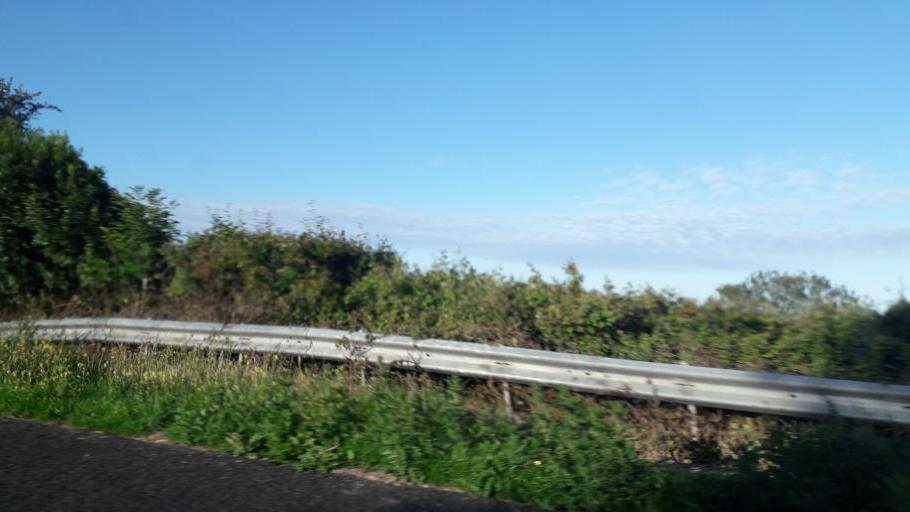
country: IE
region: Leinster
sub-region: Loch Garman
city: Loch Garman
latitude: 52.3564
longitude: -6.5063
